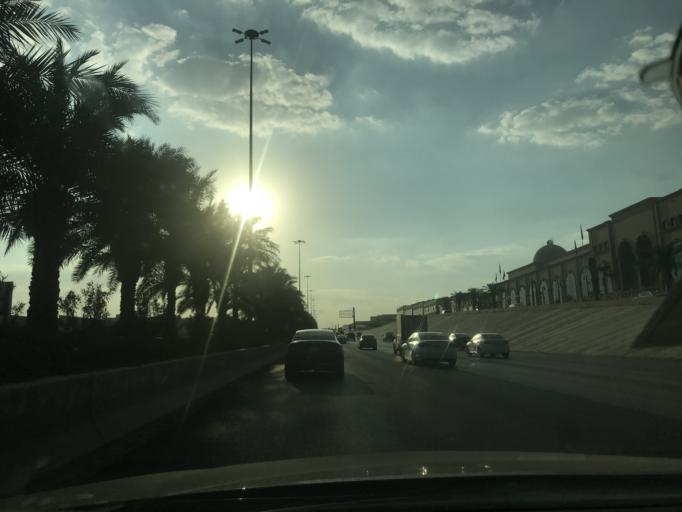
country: SA
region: Ar Riyad
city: Riyadh
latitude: 24.7460
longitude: 46.6124
